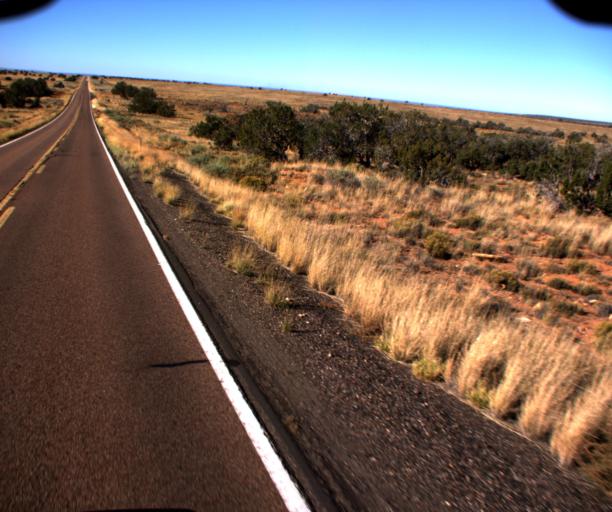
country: US
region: Arizona
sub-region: Navajo County
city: Snowflake
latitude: 34.6591
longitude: -110.3324
